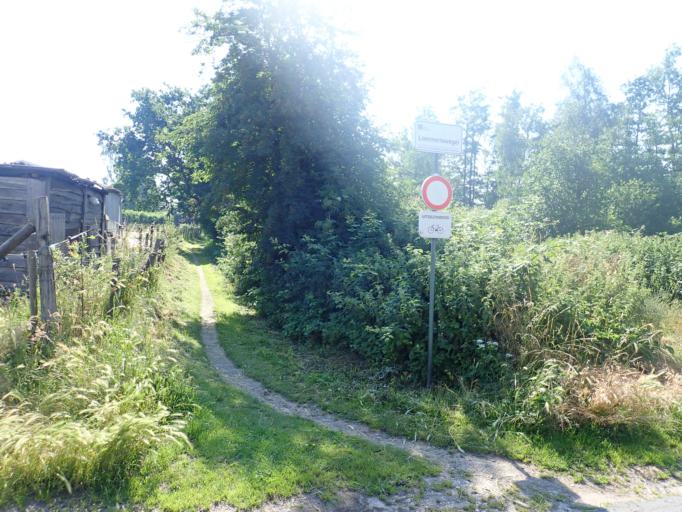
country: BE
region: Flanders
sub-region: Provincie Antwerpen
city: Zwijndrecht
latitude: 51.1992
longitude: 4.3211
